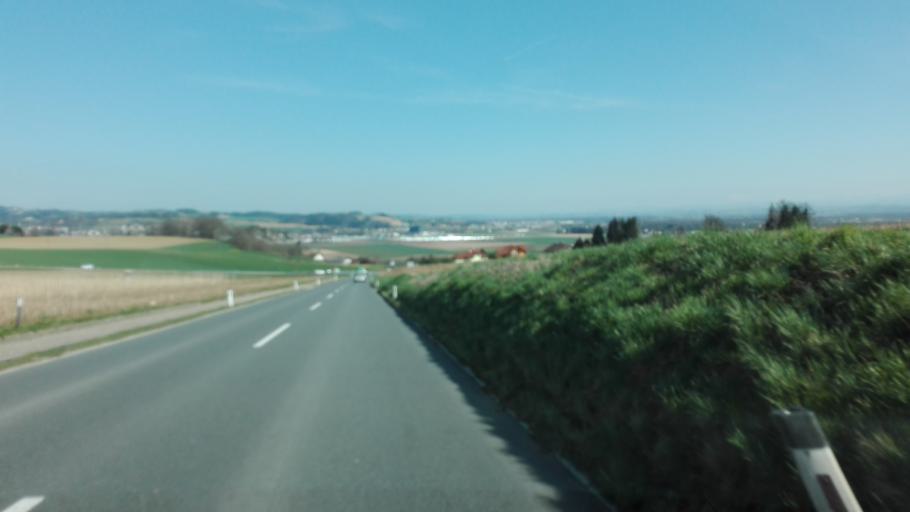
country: AT
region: Lower Austria
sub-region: Politischer Bezirk Amstetten
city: Ennsdorf
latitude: 48.2703
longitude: 14.5406
